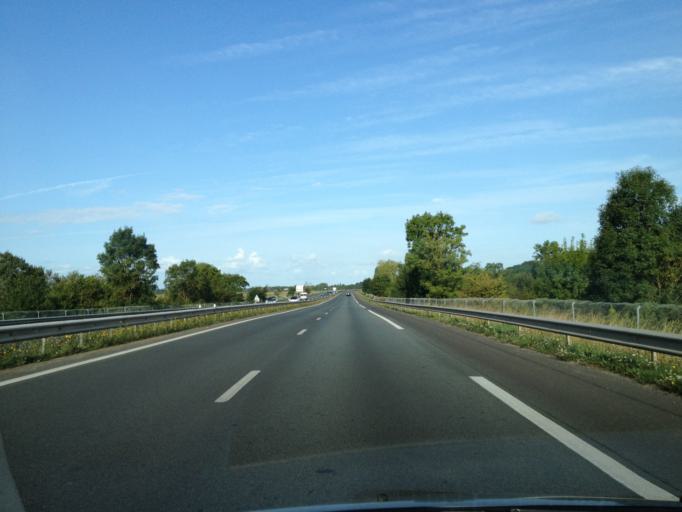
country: FR
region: Poitou-Charentes
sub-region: Departement de la Charente-Maritime
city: Saint-Laurent-de-la-Pree
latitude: 45.9805
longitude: -1.0046
